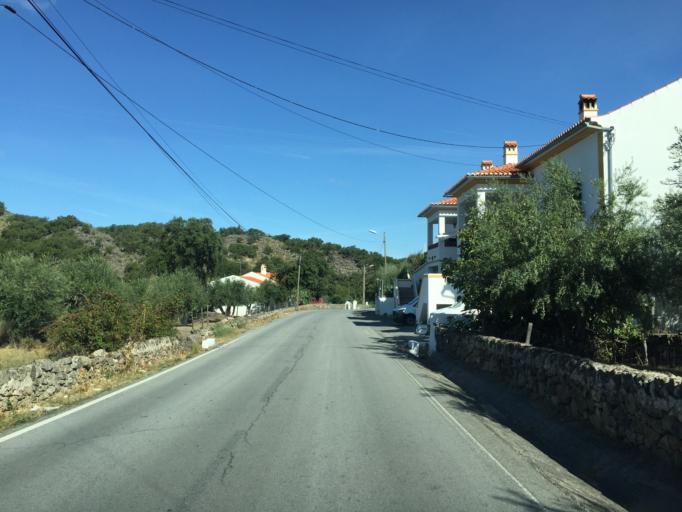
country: PT
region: Portalegre
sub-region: Marvao
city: Marvao
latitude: 39.4141
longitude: -7.3534
